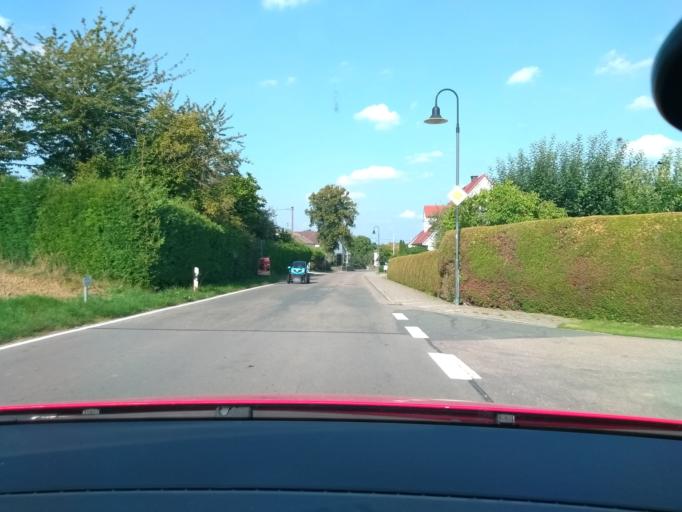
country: DE
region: Bavaria
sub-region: Upper Bavaria
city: Altomunster
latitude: 48.4037
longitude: 11.2856
